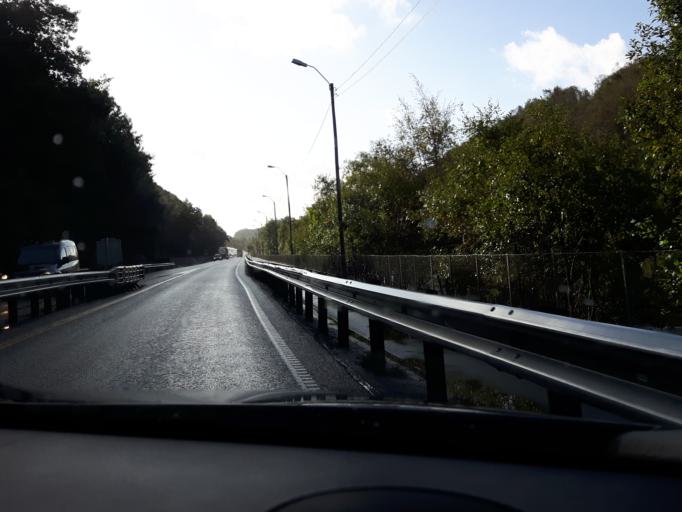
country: NO
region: Rogaland
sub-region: Gjesdal
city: Algard
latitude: 58.7953
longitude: 5.7962
